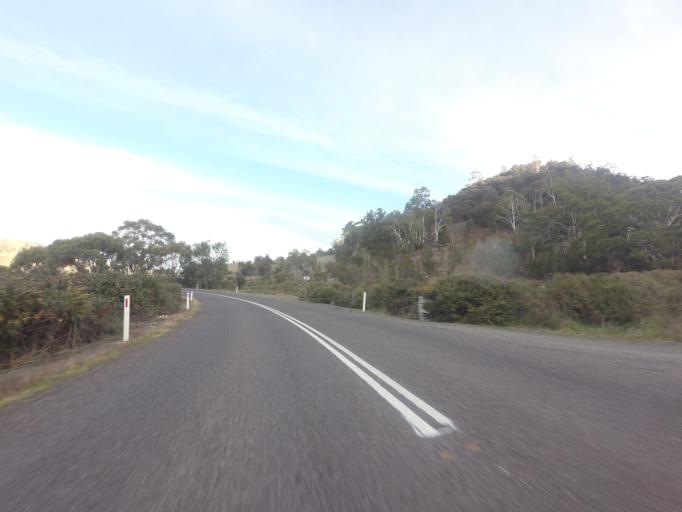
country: AU
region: Tasmania
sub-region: Brighton
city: Bridgewater
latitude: -42.4249
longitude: 147.1387
